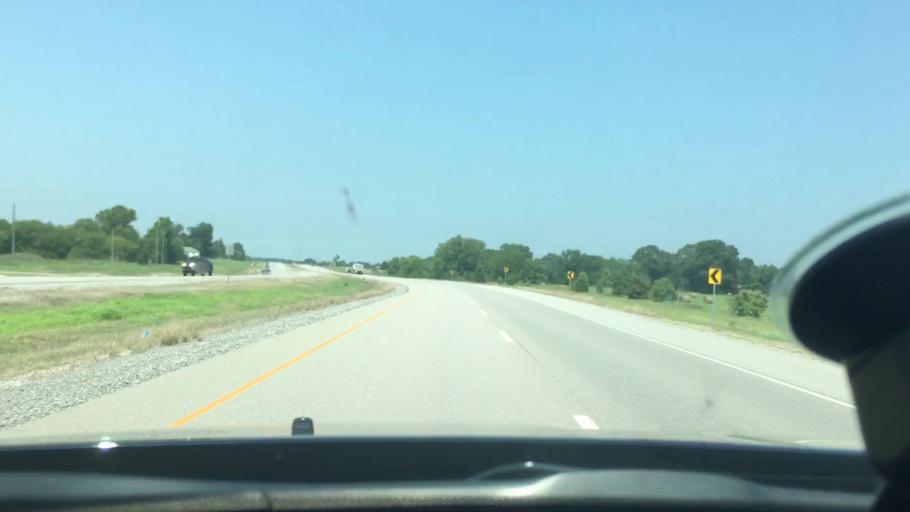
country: US
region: Oklahoma
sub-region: Atoka County
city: Atoka
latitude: 34.3343
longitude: -96.0549
